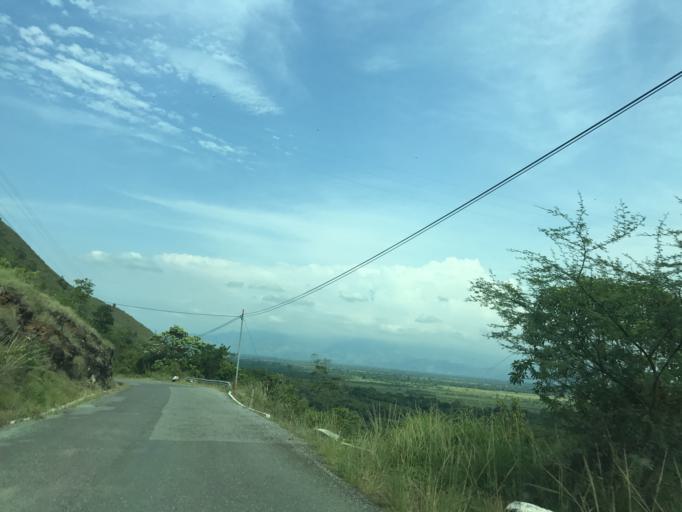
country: GT
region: Izabal
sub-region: Municipio de Los Amates
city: Los Amates
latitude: 15.3884
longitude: -89.0287
